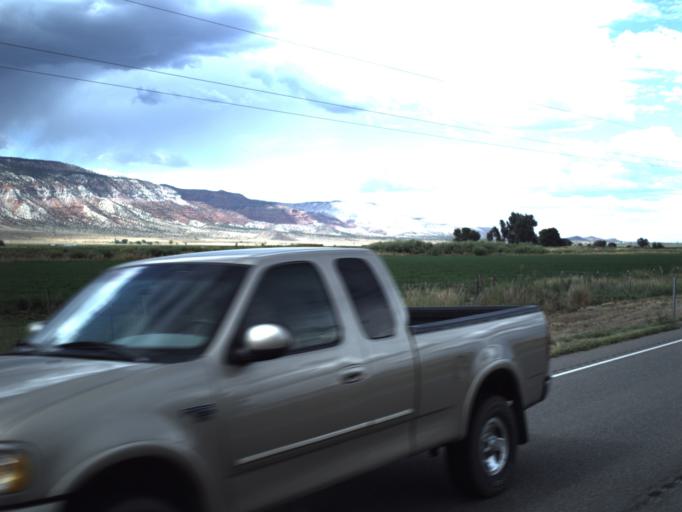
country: US
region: Utah
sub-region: Sevier County
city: Richfield
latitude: 38.7952
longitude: -112.0374
